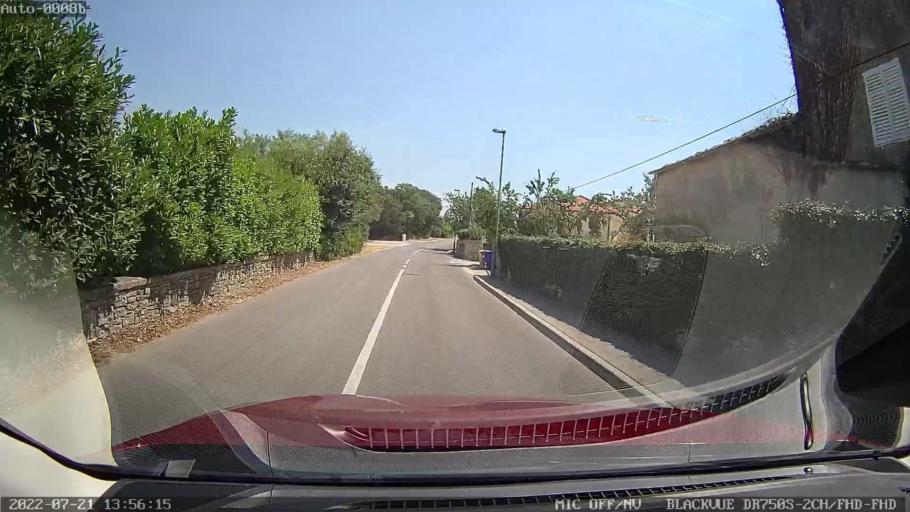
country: HR
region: Istarska
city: Pazin
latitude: 45.1203
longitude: 13.8408
